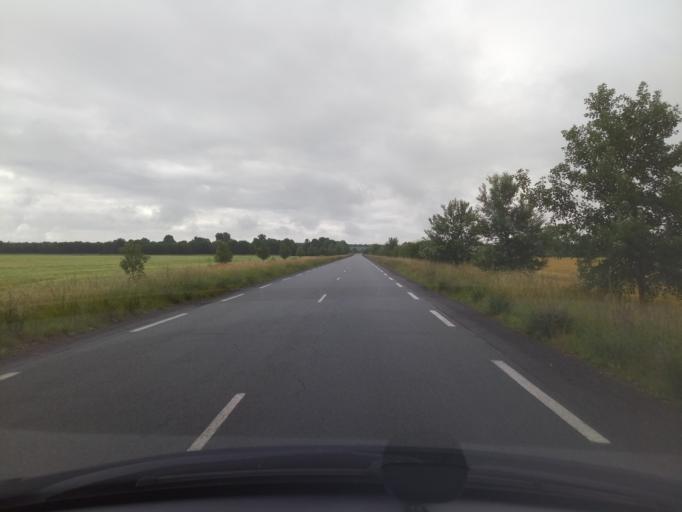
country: FR
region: Poitou-Charentes
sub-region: Departement de la Charente-Maritime
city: Courcon
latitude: 46.1932
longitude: -0.8621
